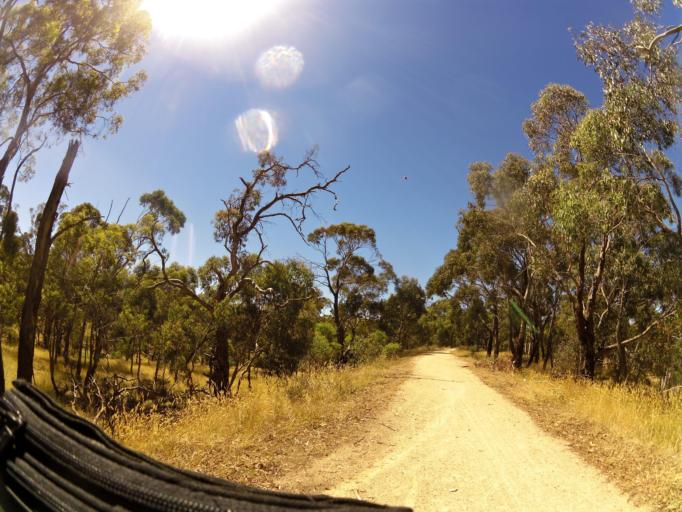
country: AU
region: Victoria
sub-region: Ballarat North
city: Delacombe
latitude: -37.7049
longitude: 143.6012
